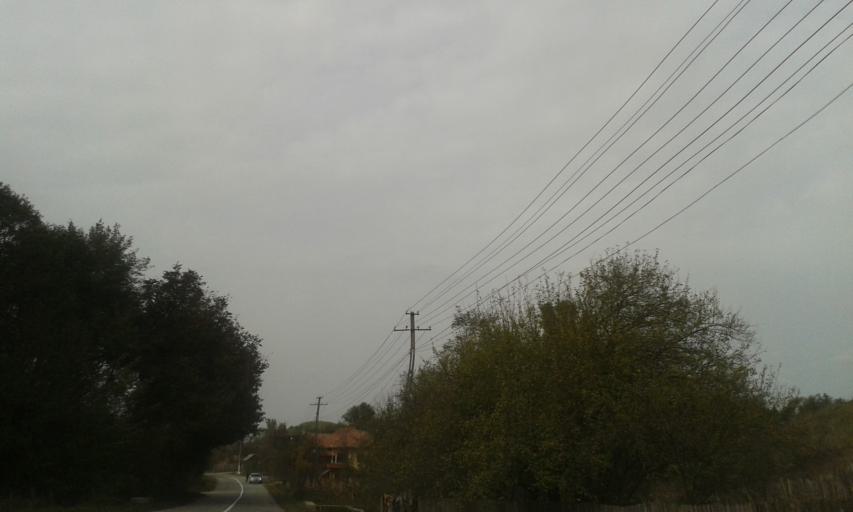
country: RO
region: Valcea
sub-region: Comuna Gradistea
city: Gradistea
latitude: 44.9063
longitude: 23.7943
